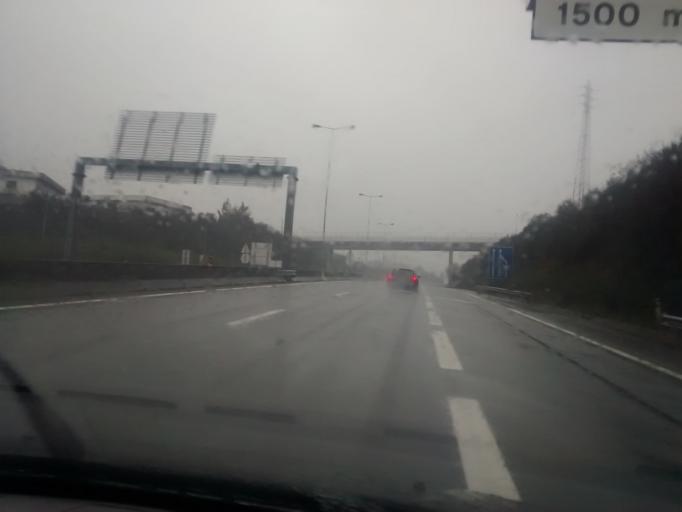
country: PT
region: Braga
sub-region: Braga
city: Braga
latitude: 41.5288
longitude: -8.4436
